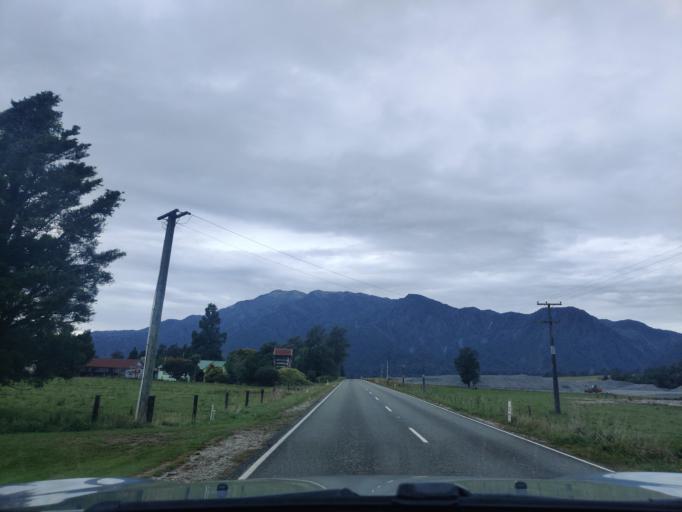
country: NZ
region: West Coast
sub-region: Westland District
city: Hokitika
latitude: -43.1535
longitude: 170.5891
